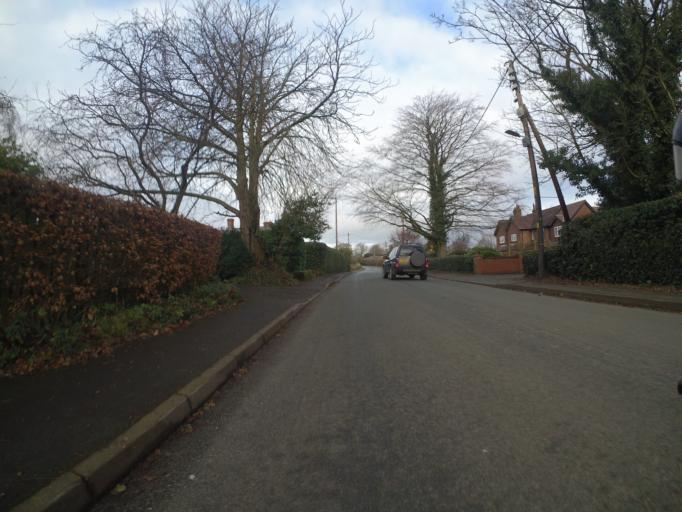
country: GB
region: England
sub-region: Cheshire West and Chester
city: Tiverton
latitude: 53.1186
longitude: -2.6581
